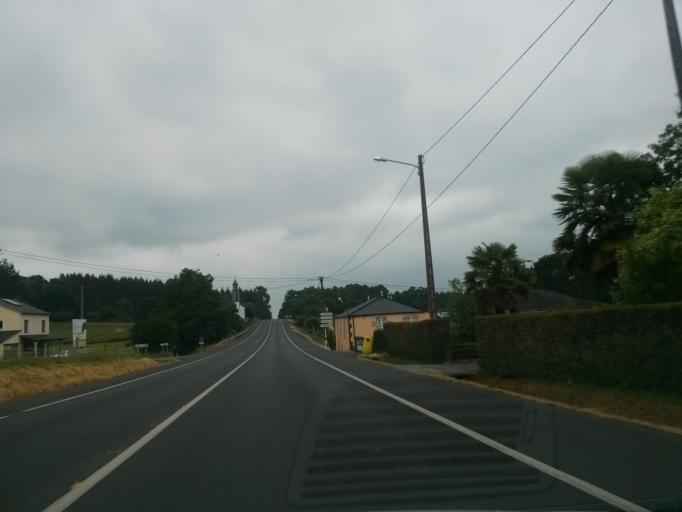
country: ES
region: Galicia
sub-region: Provincia de Lugo
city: Begonte
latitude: 43.1429
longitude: -7.6745
